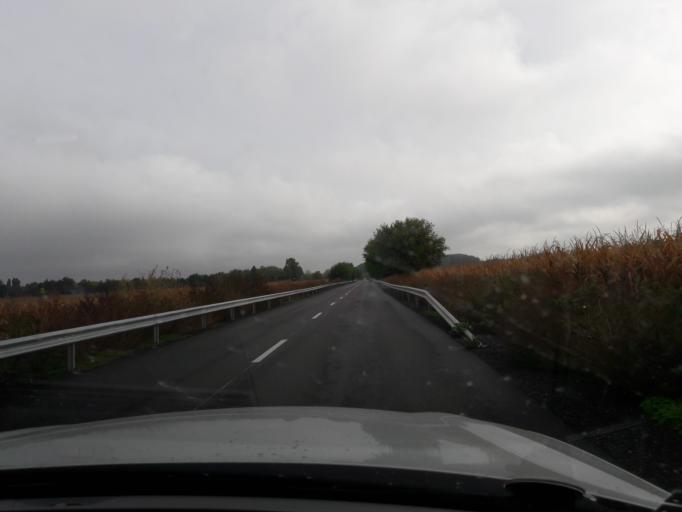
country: SK
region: Nitriansky
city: Tlmace
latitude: 48.1904
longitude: 18.5014
